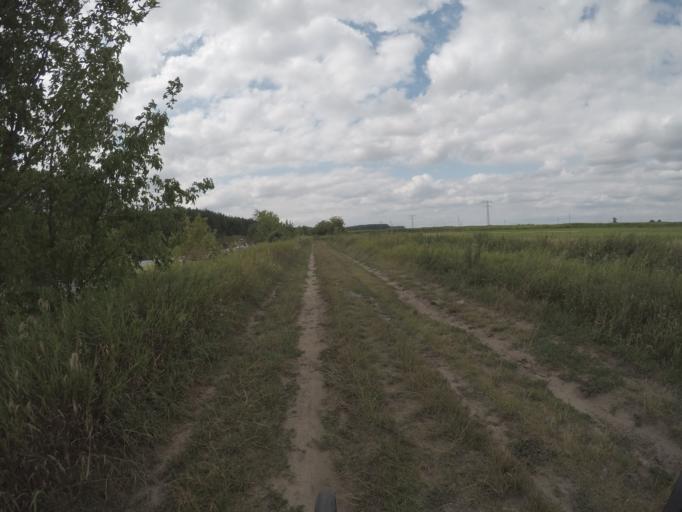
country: DE
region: Brandenburg
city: Falkensee
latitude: 52.6074
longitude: 13.0708
